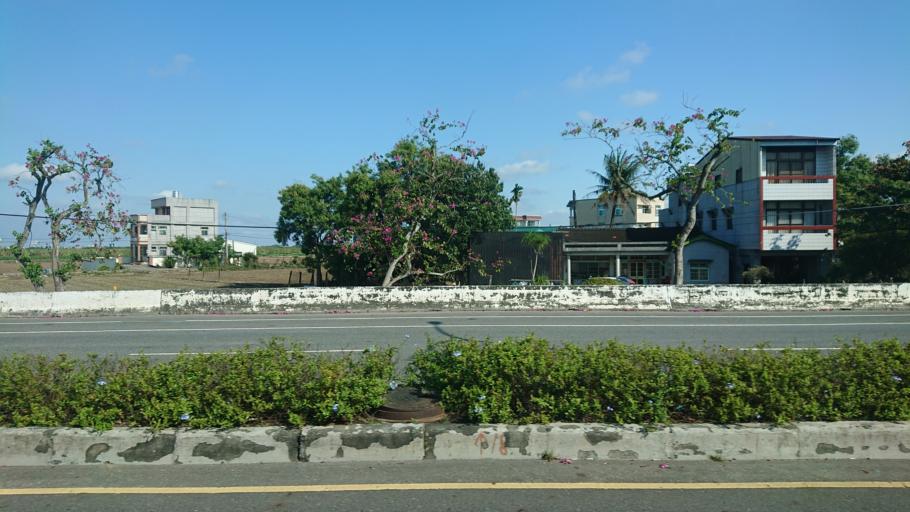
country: TW
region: Taiwan
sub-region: Chiayi
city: Taibao
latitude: 23.4420
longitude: 120.3769
